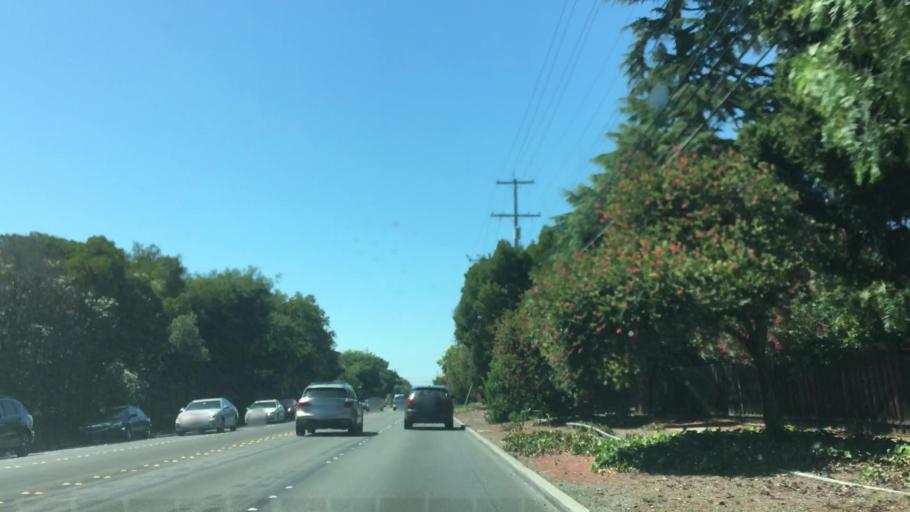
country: US
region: California
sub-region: Santa Clara County
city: Los Altos
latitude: 37.4157
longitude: -122.1198
